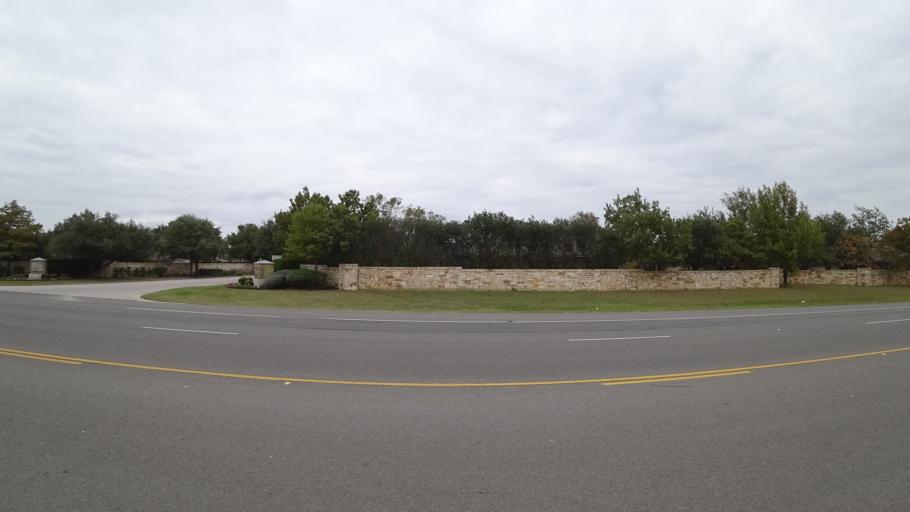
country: US
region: Texas
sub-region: Travis County
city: Bee Cave
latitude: 30.3083
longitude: -97.9235
